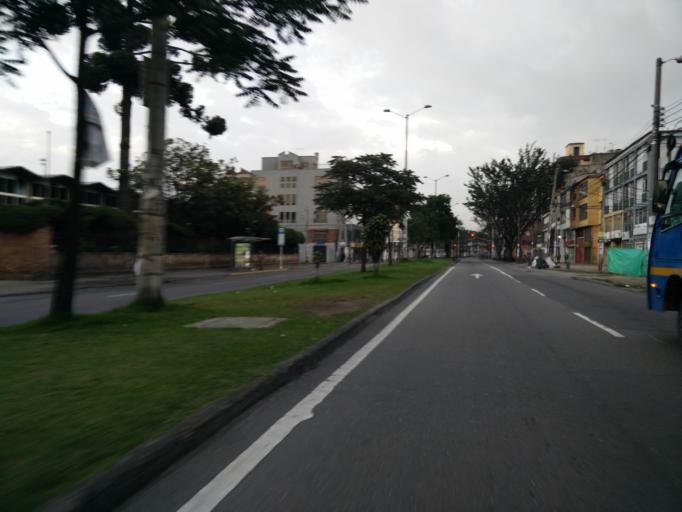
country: CO
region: Bogota D.C.
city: Bogota
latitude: 4.6541
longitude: -74.0719
